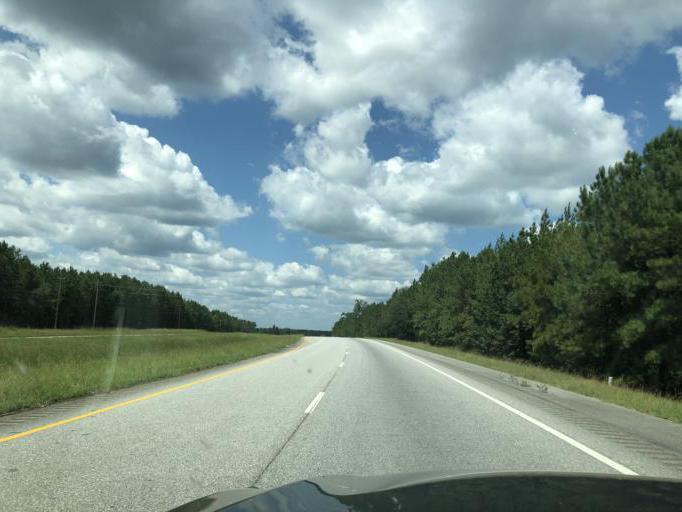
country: US
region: Alabama
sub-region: Russell County
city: Ladonia
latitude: 32.2179
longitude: -85.1684
